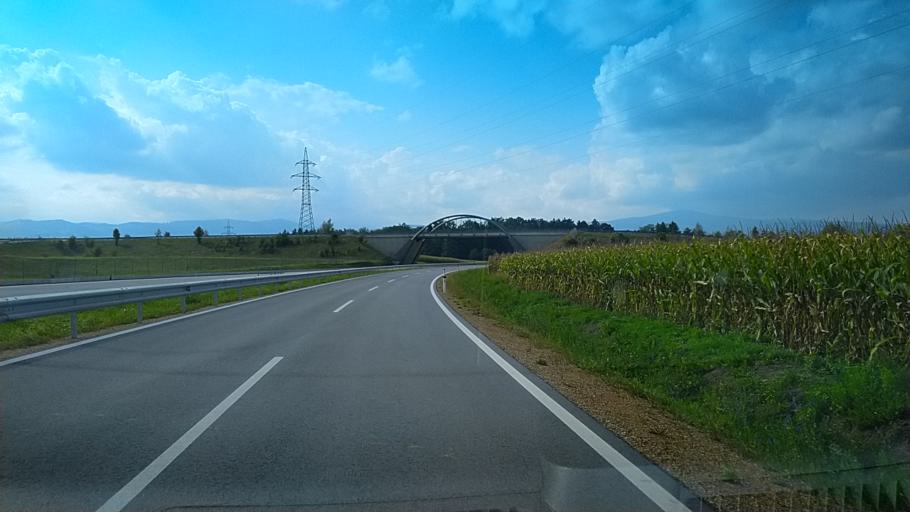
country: AT
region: Styria
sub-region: Politischer Bezirk Deutschlandsberg
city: Unterbergla
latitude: 46.8143
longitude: 15.2902
